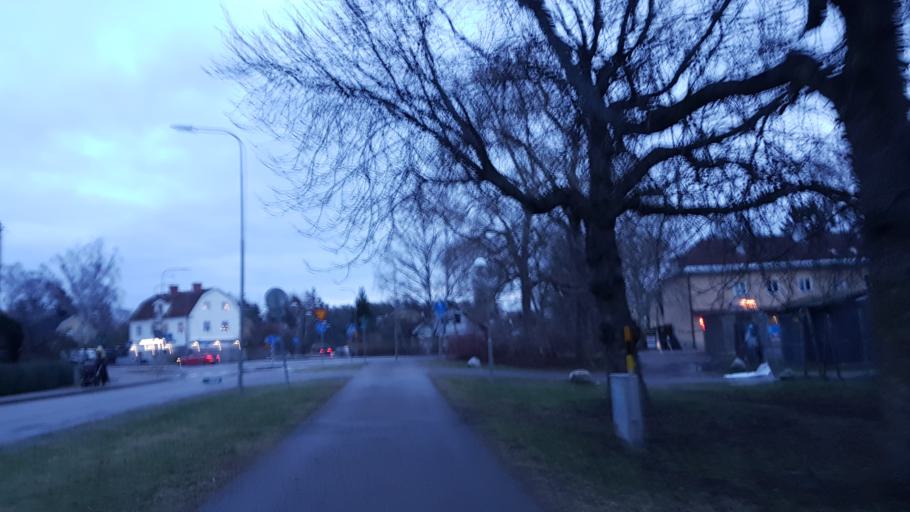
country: SE
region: Stockholm
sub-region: Stockholms Kommun
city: Arsta
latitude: 59.2803
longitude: 18.0497
